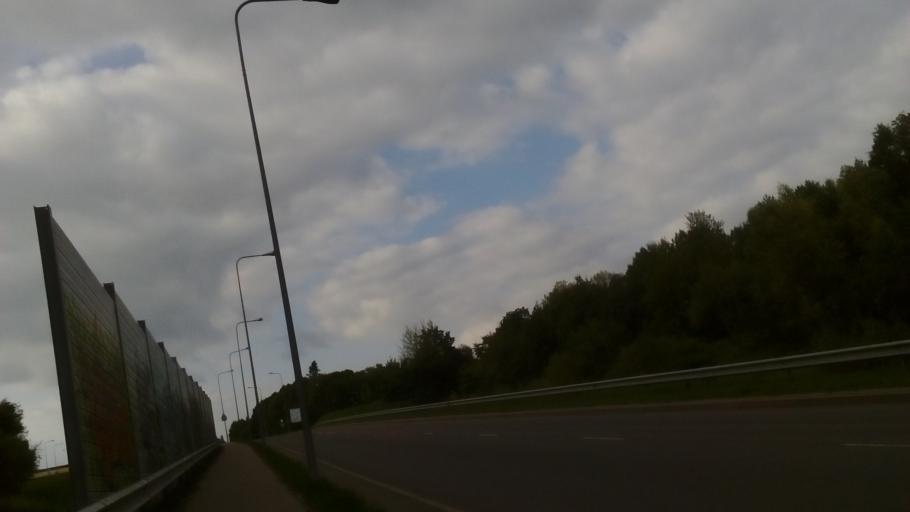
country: LT
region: Alytaus apskritis
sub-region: Alytus
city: Alytus
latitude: 54.4231
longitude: 24.0356
